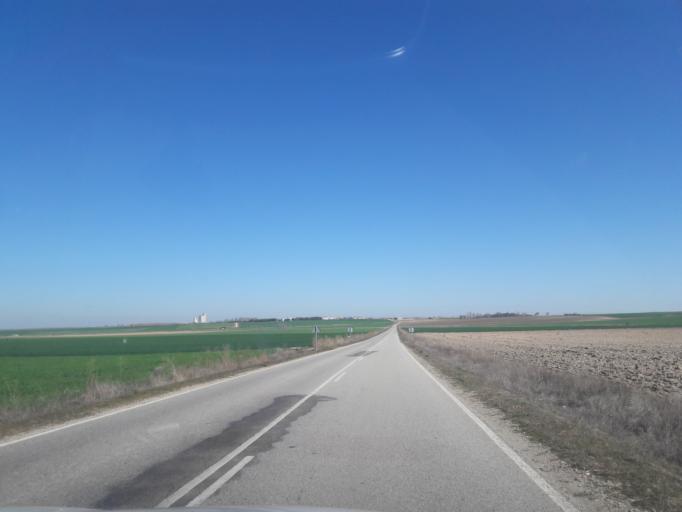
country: ES
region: Castille and Leon
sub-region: Provincia de Salamanca
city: Boveda del Rio Almar
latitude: 40.8679
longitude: -5.1984
